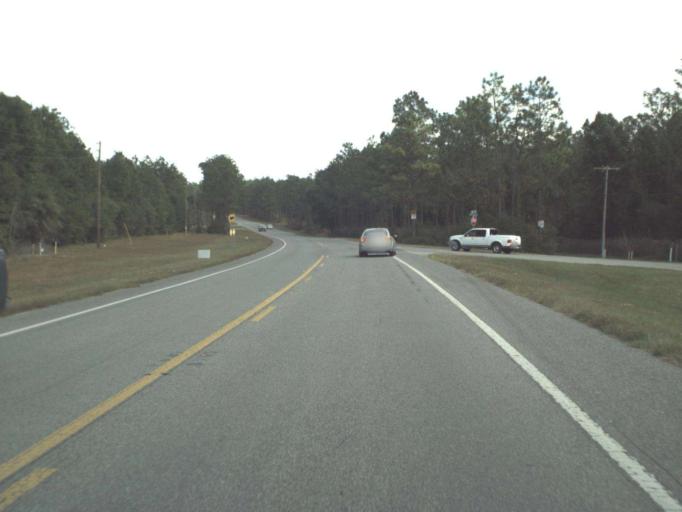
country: US
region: Florida
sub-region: Okaloosa County
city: Crestview
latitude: 30.7214
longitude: -86.6761
